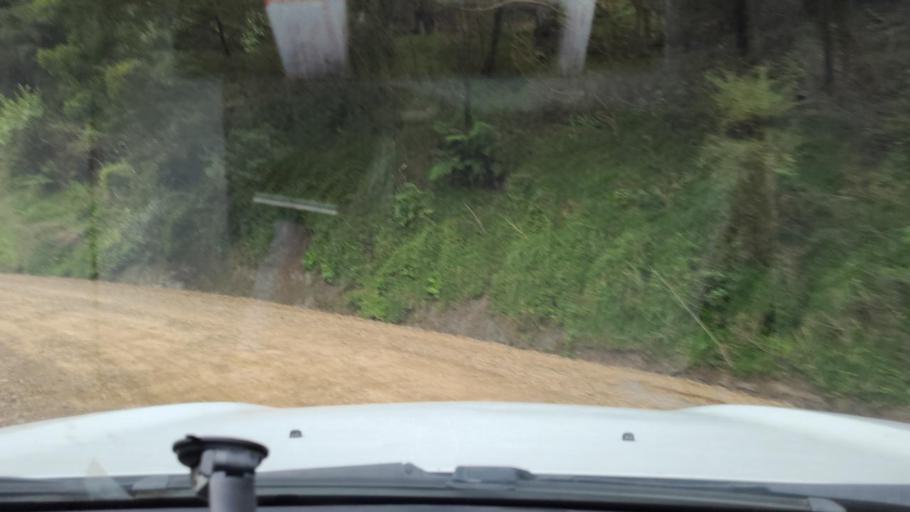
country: NZ
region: Gisborne
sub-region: Gisborne District
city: Gisborne
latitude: -38.5779
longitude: 178.0333
